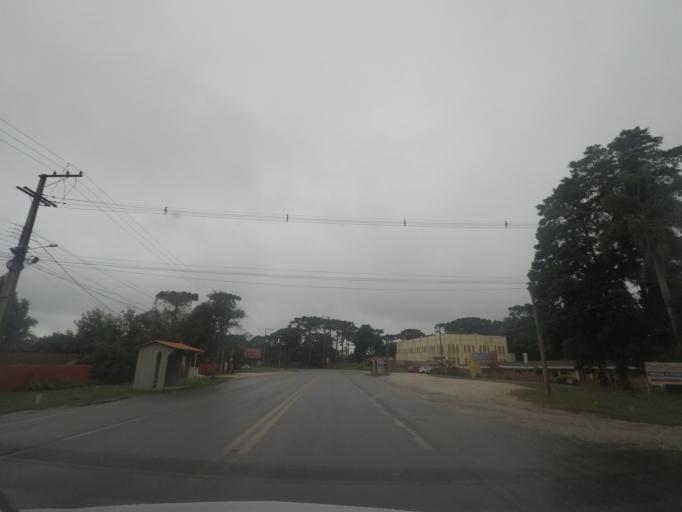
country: BR
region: Parana
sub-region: Colombo
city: Colombo
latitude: -25.3081
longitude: -49.1438
